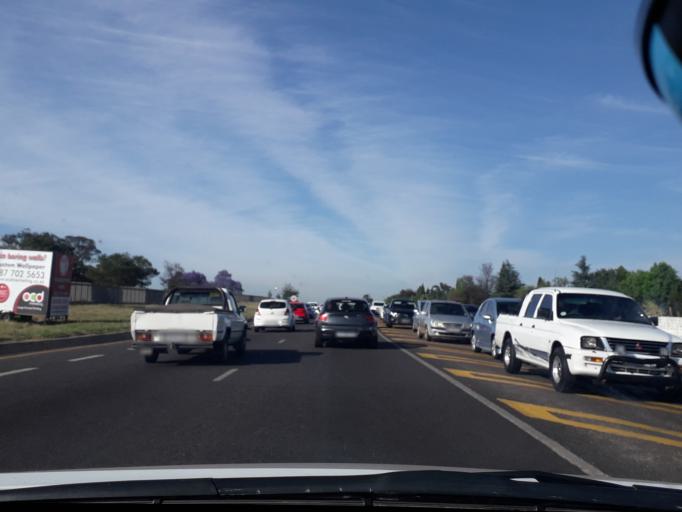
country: ZA
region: Gauteng
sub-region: City of Johannesburg Metropolitan Municipality
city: Roodepoort
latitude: -26.1056
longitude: 27.9241
